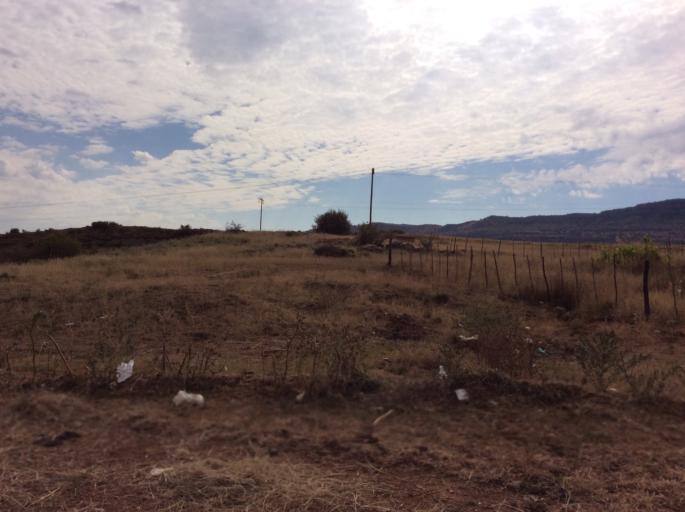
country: LS
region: Mafeteng
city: Mafeteng
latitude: -29.7205
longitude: 27.0085
